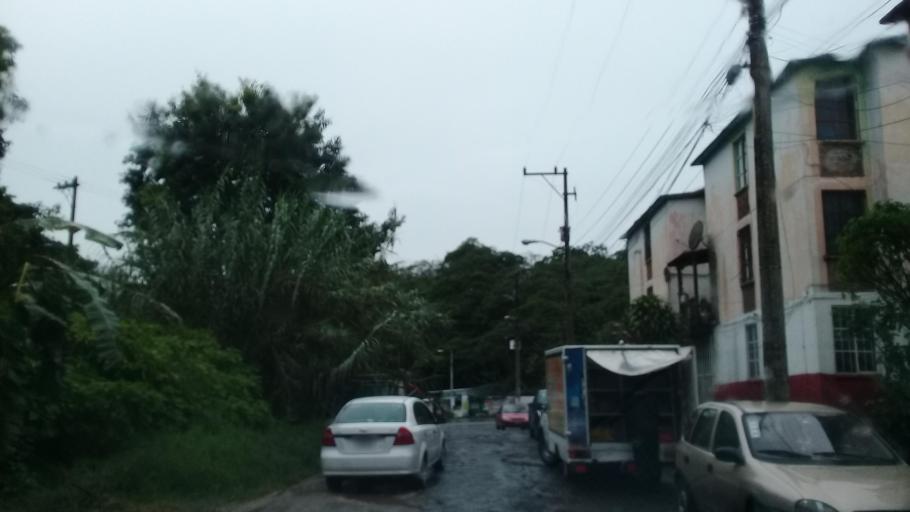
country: MX
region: Veracruz
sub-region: Xalapa
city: Lomas Verdes
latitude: 19.5130
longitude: -96.8998
